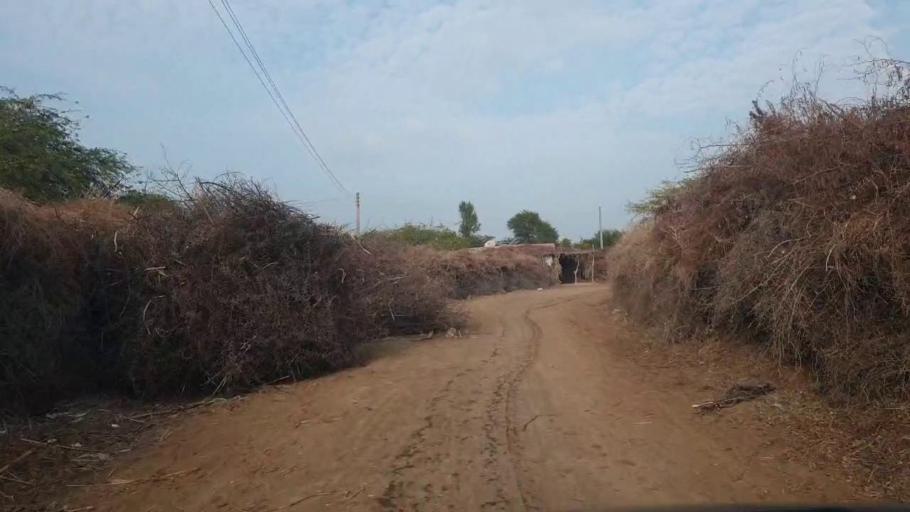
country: PK
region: Sindh
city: Shahdadpur
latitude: 25.8844
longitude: 68.7233
